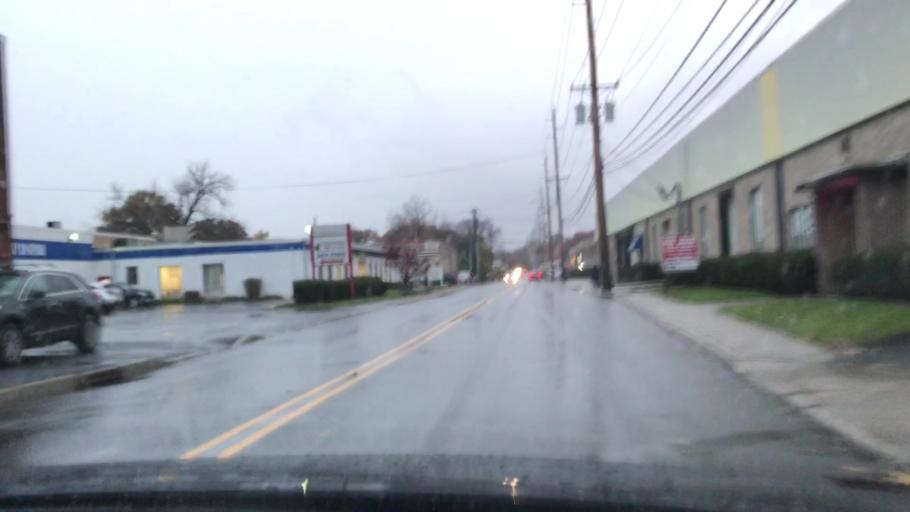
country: US
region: New Jersey
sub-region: Bergen County
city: Bergenfield
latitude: 40.9158
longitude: -74.0007
